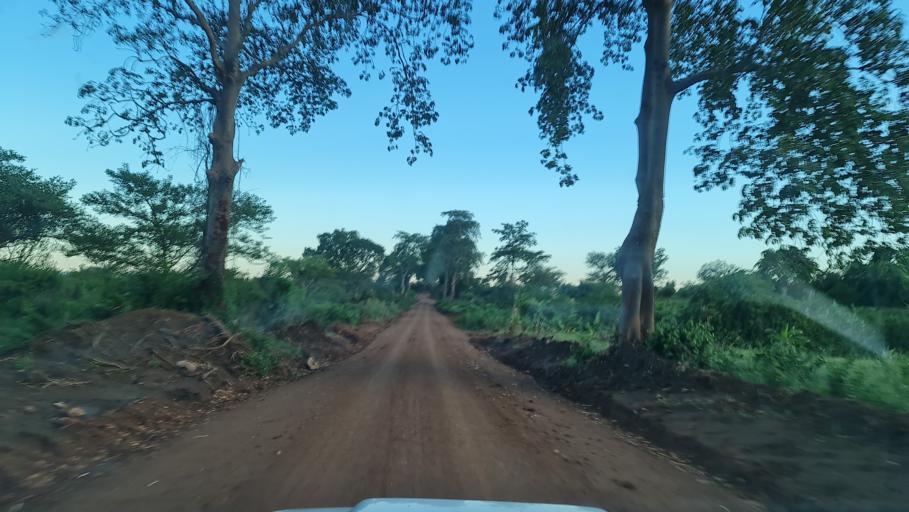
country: MZ
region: Nampula
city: Ilha de Mocambique
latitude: -14.9795
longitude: 40.0934
